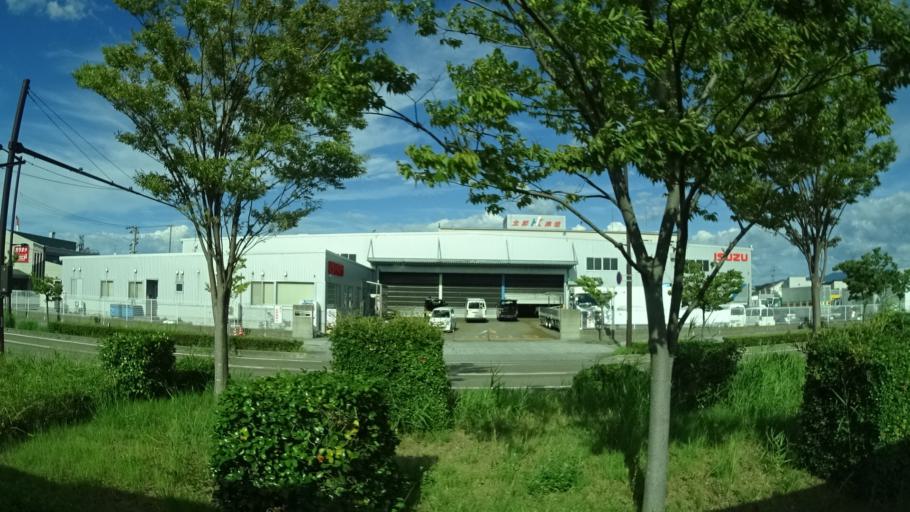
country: JP
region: Ishikawa
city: Kanazawa-shi
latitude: 36.6056
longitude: 136.6186
